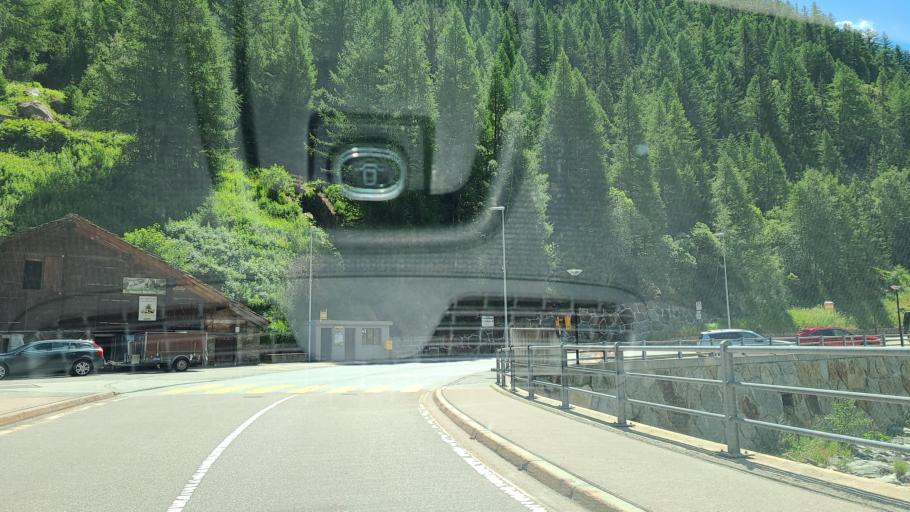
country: CH
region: Valais
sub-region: Visp District
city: Saas-Grund
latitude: 46.1535
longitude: 7.9280
